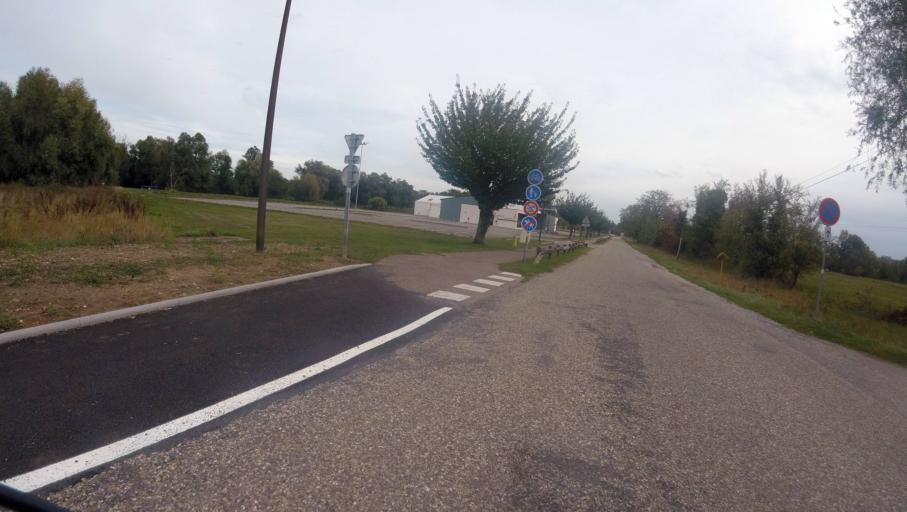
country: DE
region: Baden-Wuerttemberg
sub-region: Karlsruhe Region
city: Steinmauern
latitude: 48.9335
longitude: 8.1608
